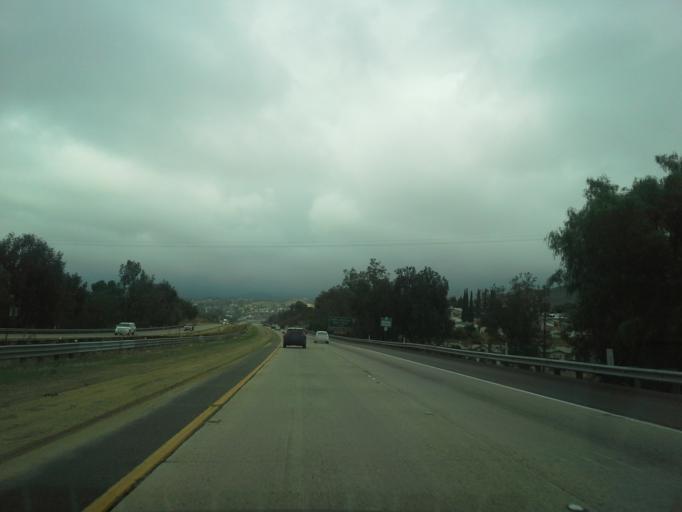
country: US
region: California
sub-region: San Diego County
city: Granite Hills
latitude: 32.8307
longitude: -116.8977
